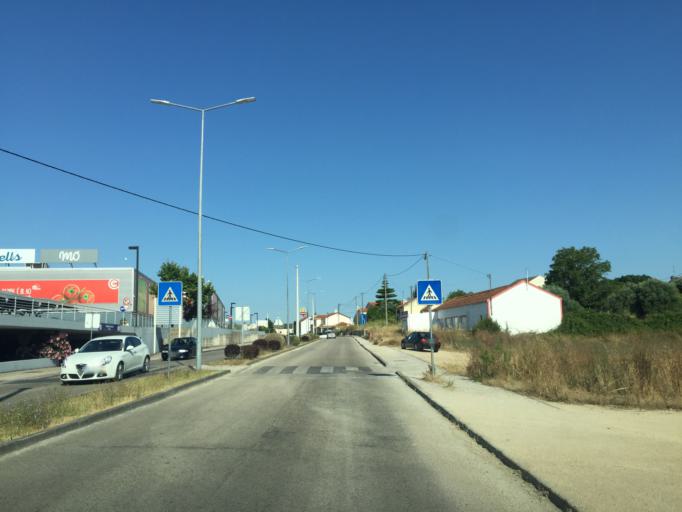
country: PT
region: Santarem
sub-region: Tomar
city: Tomar
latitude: 39.6023
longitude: -8.3958
